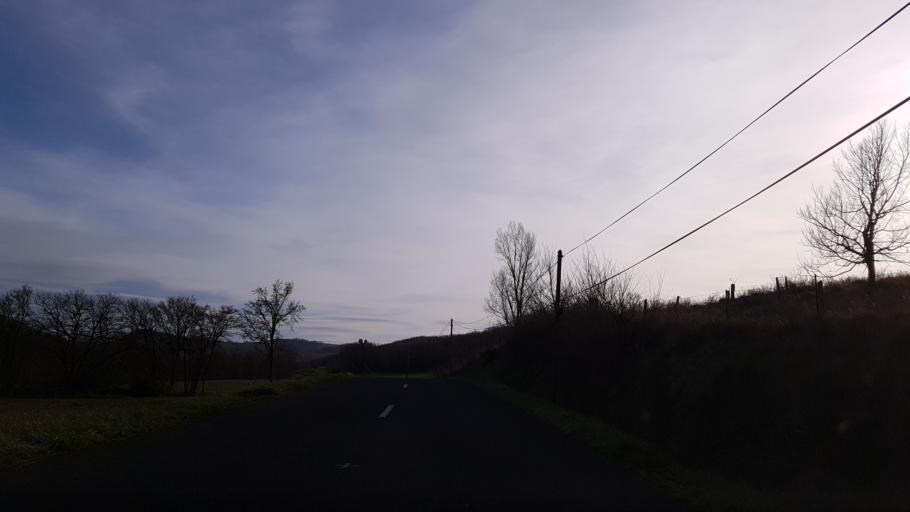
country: FR
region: Midi-Pyrenees
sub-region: Departement de l'Ariege
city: Mirepoix
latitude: 43.1689
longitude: 1.9097
